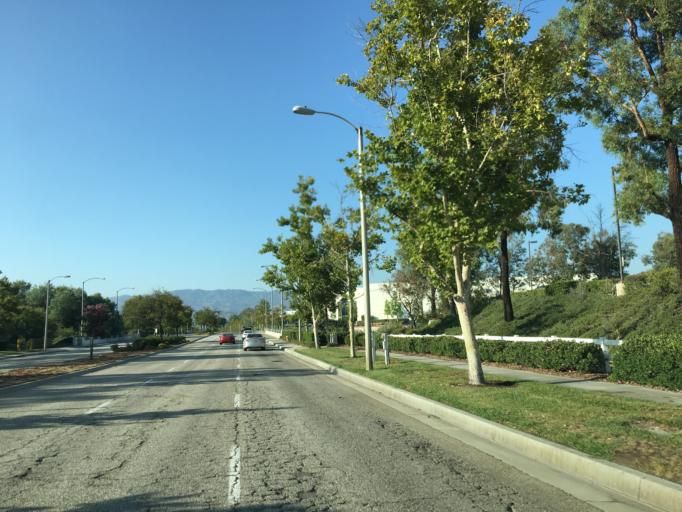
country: US
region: California
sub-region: Los Angeles County
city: Valencia
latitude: 34.4486
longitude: -118.6263
